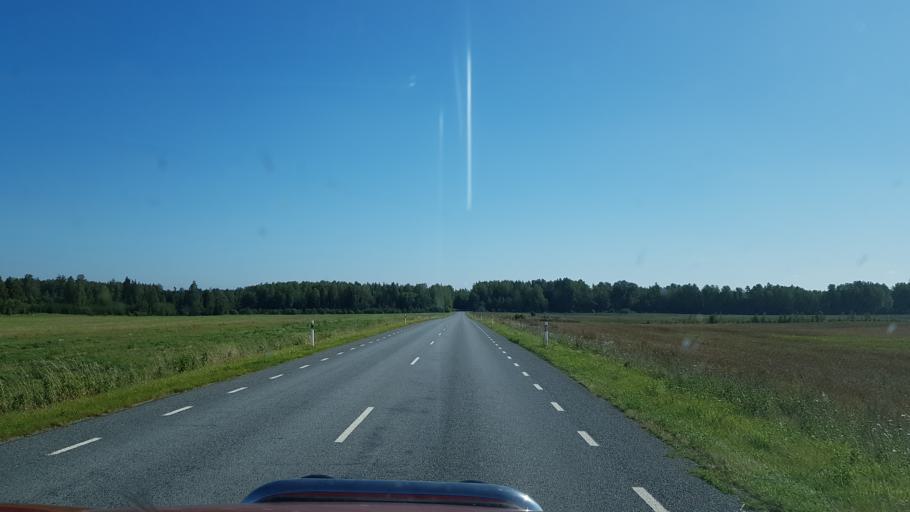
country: EE
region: Polvamaa
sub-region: Polva linn
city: Polva
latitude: 58.2767
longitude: 27.0761
